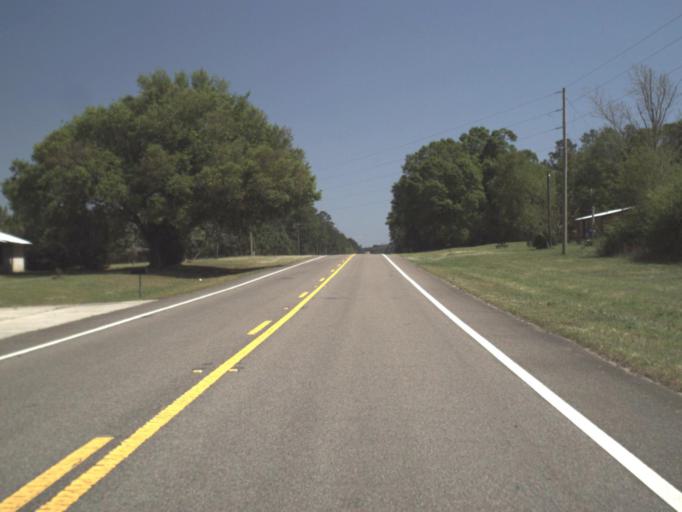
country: US
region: Florida
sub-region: Santa Rosa County
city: Point Baker
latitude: 30.8925
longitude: -86.9814
